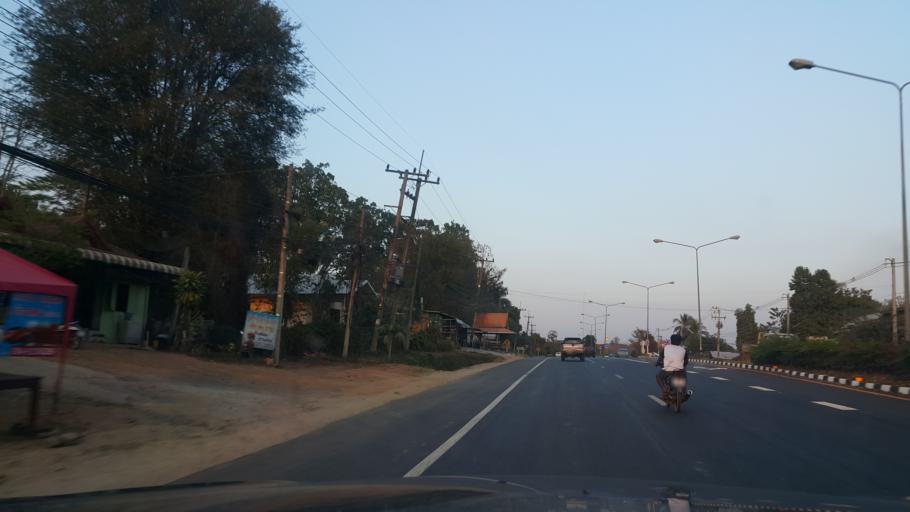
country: TH
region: Loei
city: Loei
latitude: 17.4913
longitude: 101.7042
